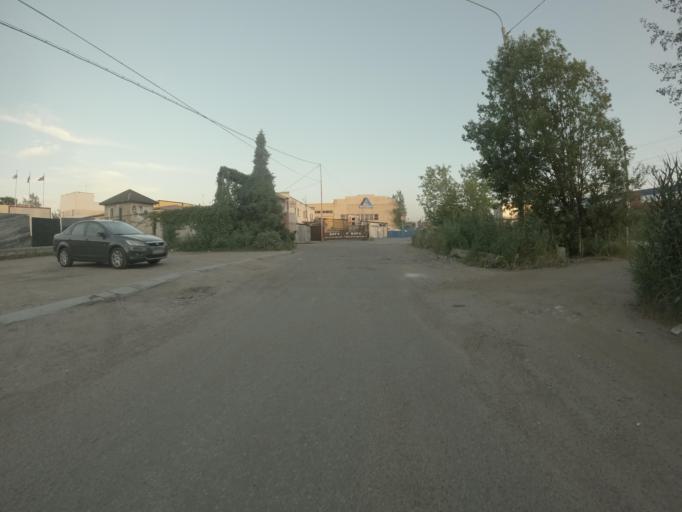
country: RU
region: St.-Petersburg
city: Krasnogvargeisky
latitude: 59.9440
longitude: 30.4483
